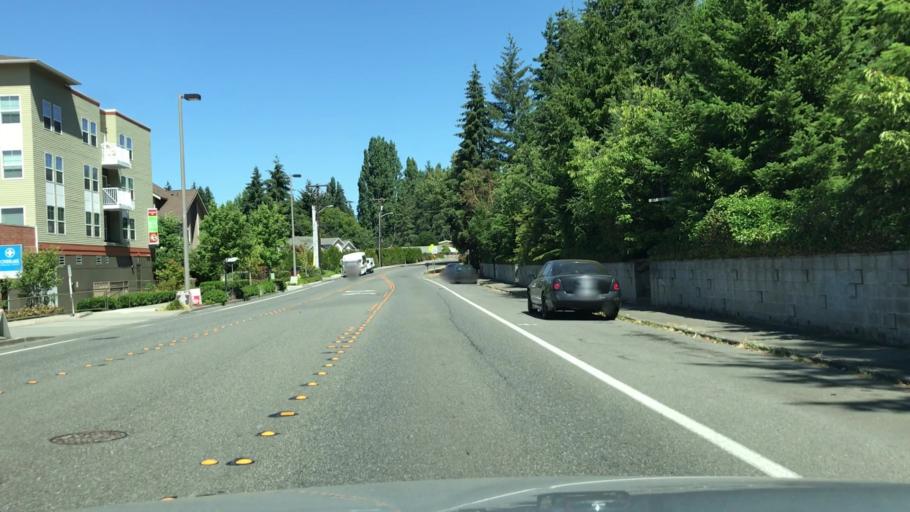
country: US
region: Washington
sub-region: King County
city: Eastgate
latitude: 47.6045
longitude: -122.1314
